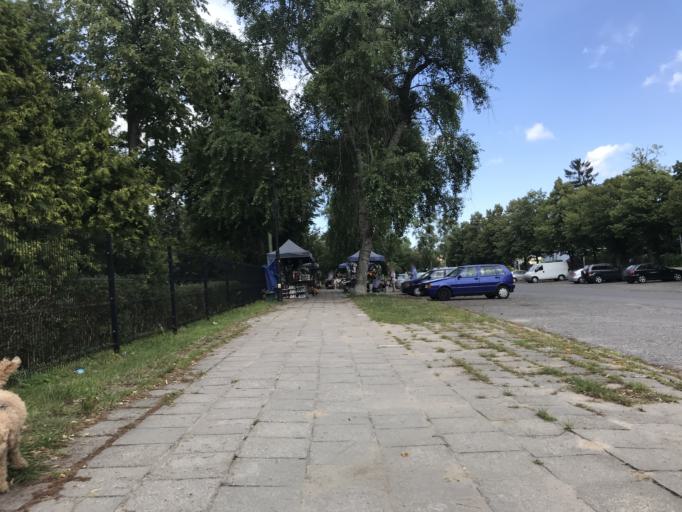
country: PL
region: Warmian-Masurian Voivodeship
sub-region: Powiat elblaski
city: Elblag
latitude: 54.1684
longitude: 19.4238
